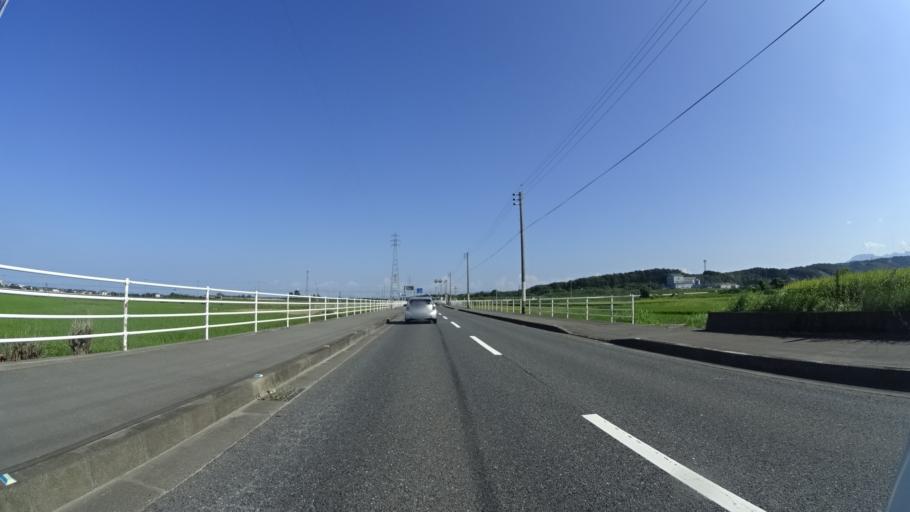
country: JP
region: Fukuoka
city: Shiida
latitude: 33.6463
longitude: 131.0578
